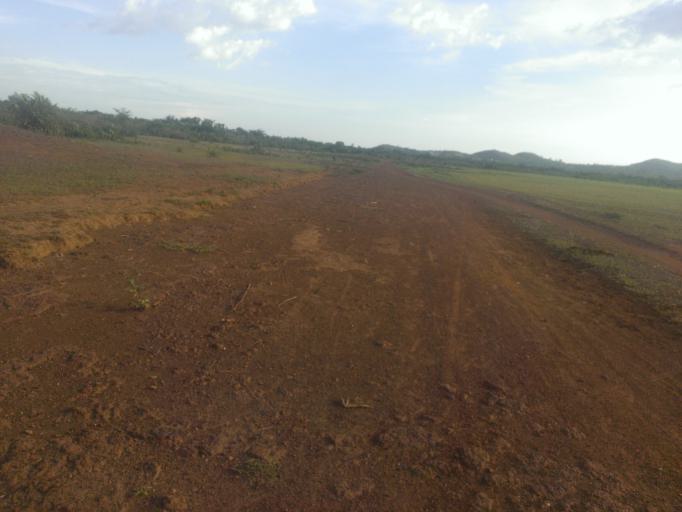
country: UG
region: Eastern Region
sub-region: Busia District
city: Busia
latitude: 0.5480
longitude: 33.9851
